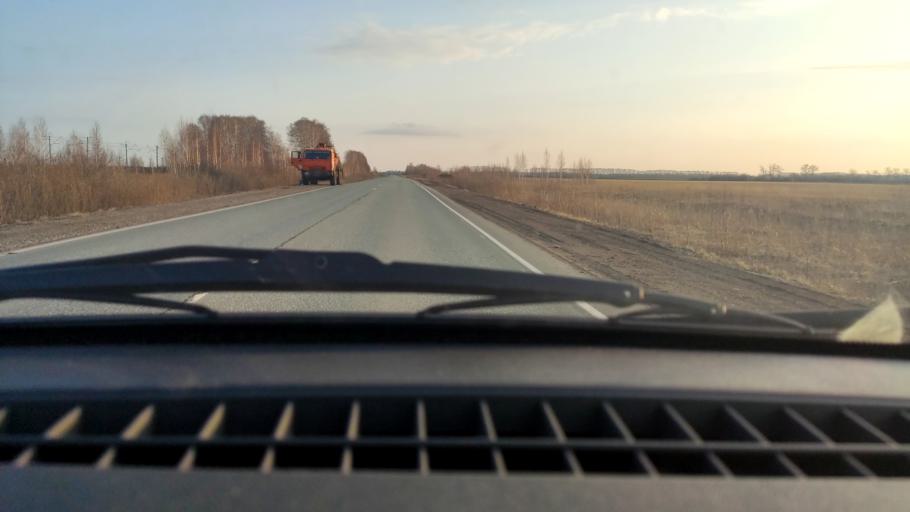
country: RU
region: Bashkortostan
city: Chishmy
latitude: 54.4205
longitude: 55.2281
